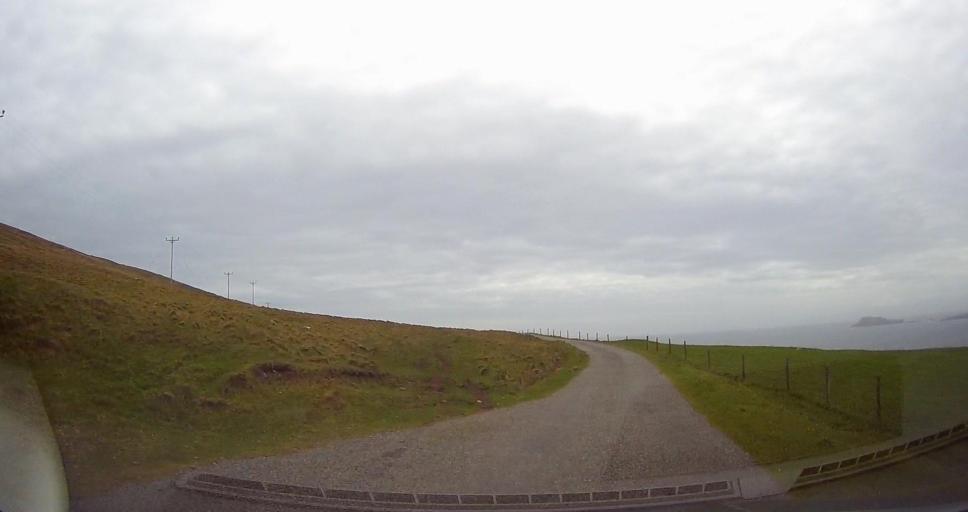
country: GB
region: Scotland
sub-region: Shetland Islands
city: Sandwick
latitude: 59.8636
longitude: -1.2774
